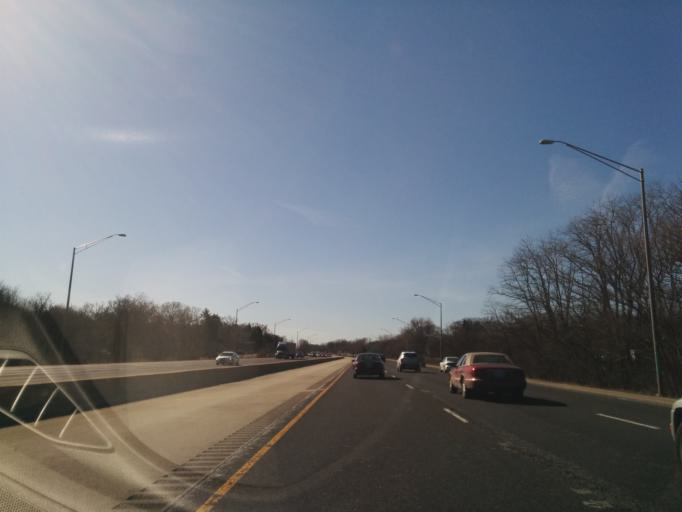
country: US
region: Illinois
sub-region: DuPage County
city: Darien
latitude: 41.7277
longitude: -87.9840
